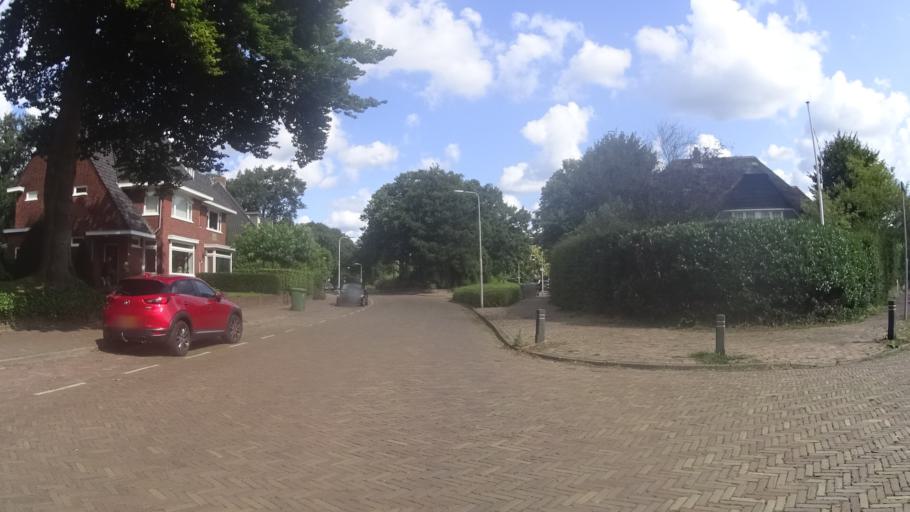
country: NL
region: North Holland
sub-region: Gemeente Bloemendaal
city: Bloemendaal
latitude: 52.4209
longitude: 4.6324
